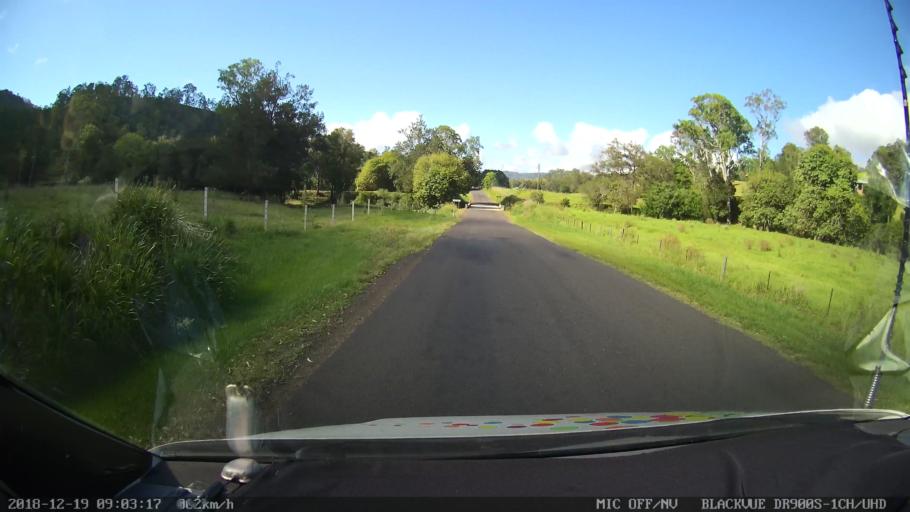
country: AU
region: New South Wales
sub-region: Kyogle
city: Kyogle
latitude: -28.4463
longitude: 152.9515
